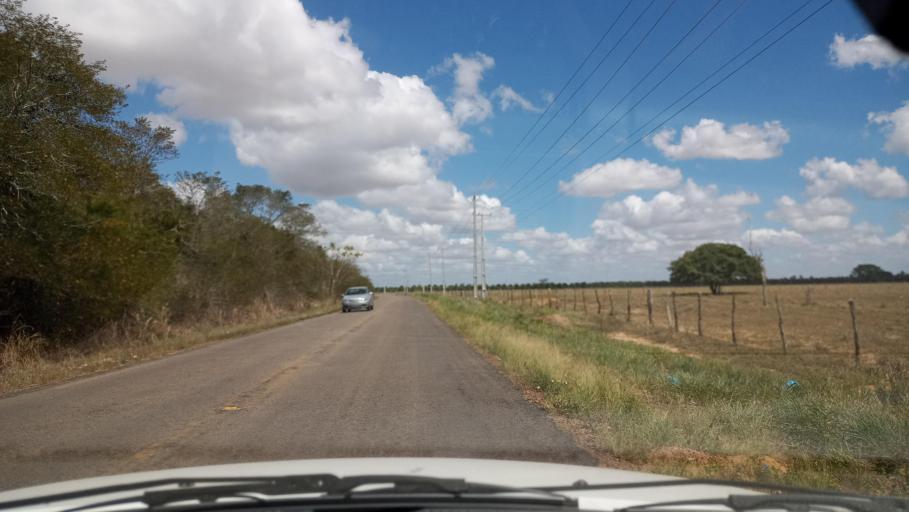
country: BR
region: Rio Grande do Norte
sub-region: Brejinho
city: Brejinho
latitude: -6.0411
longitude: -35.4136
